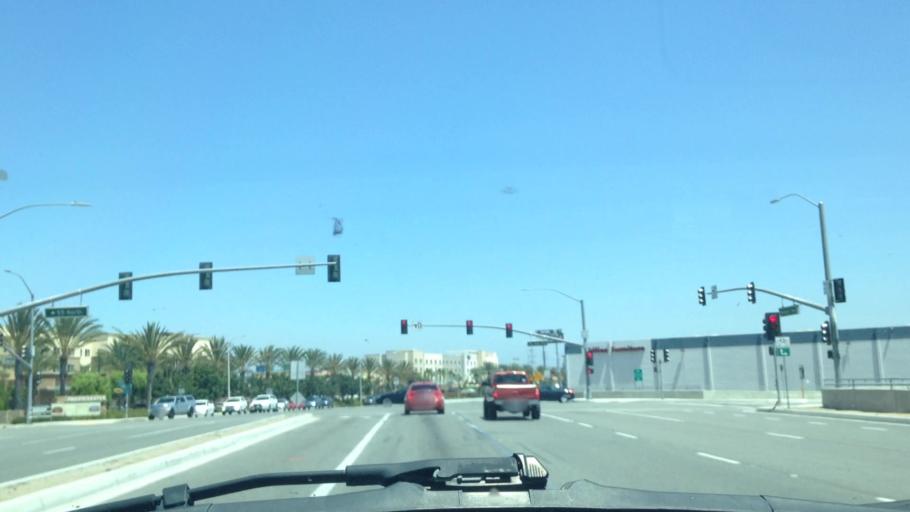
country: US
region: California
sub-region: Orange County
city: Tustin
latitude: 33.7219
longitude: -117.8352
